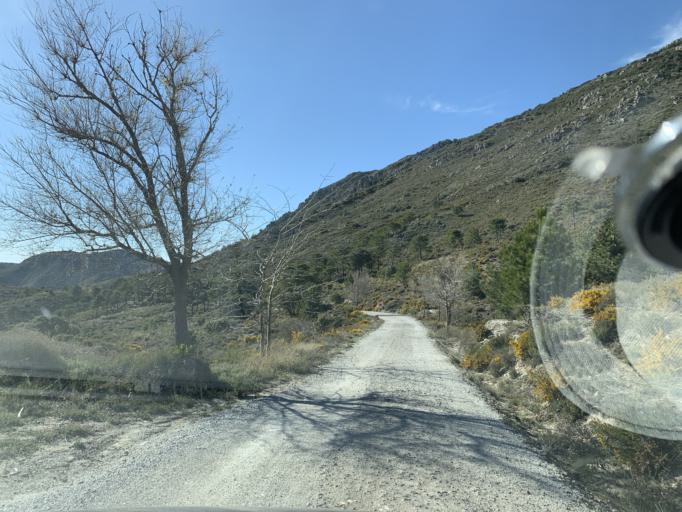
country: ES
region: Andalusia
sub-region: Provincia de Granada
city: Beas de Granada
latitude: 37.2414
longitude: -3.4488
